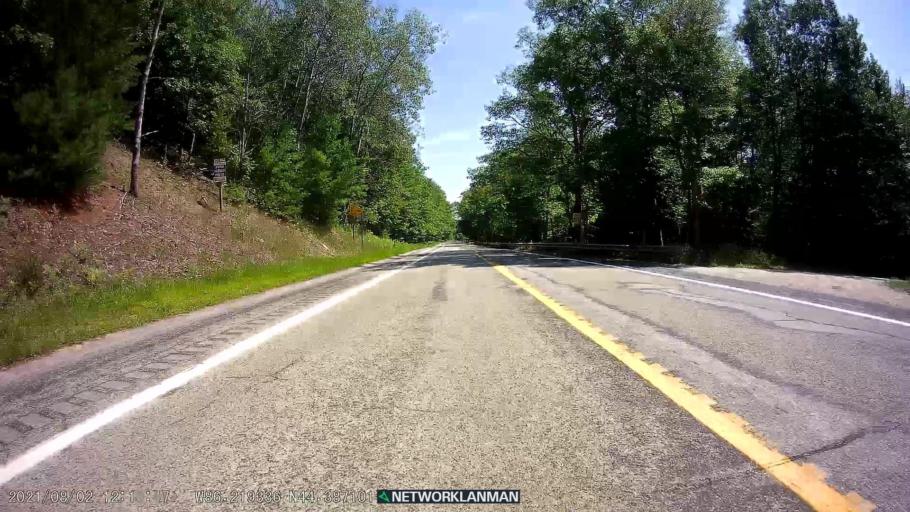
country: US
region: Michigan
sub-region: Manistee County
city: Manistee
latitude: 44.3871
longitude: -86.2200
